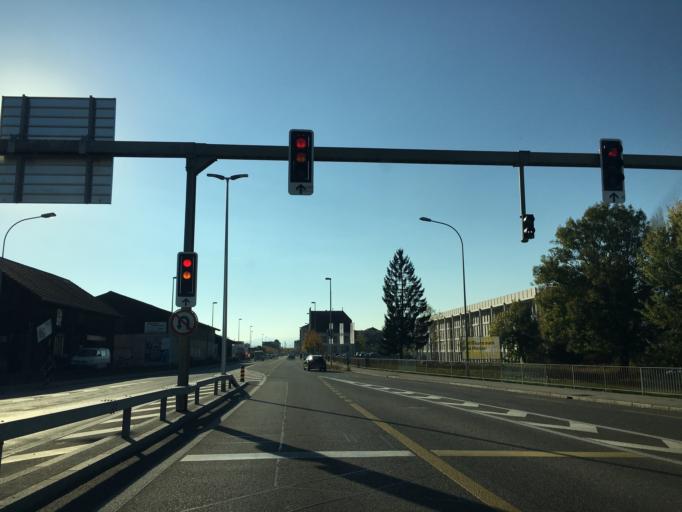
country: CH
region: Solothurn
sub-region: Bezirk Wasseramt
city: Zuchwil
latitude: 47.2059
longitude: 7.5526
